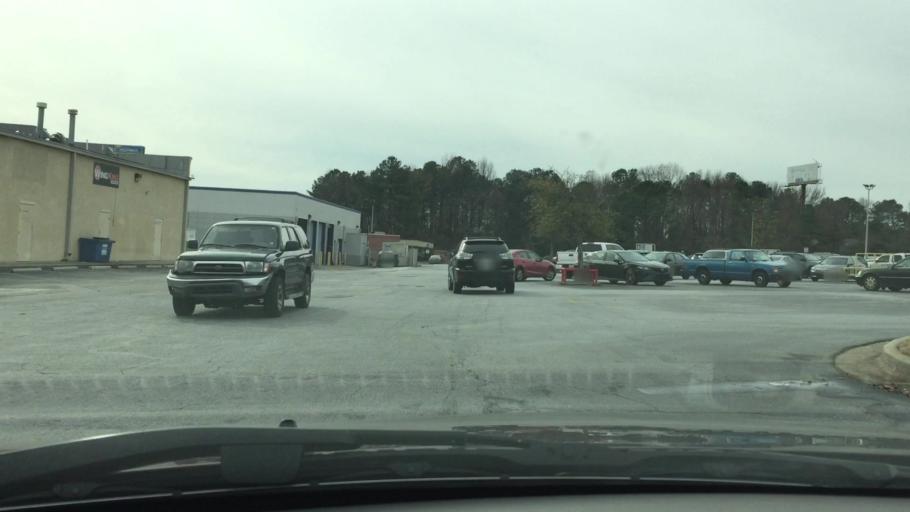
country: US
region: Georgia
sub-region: DeKalb County
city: Doraville
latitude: 33.9055
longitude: -84.2721
